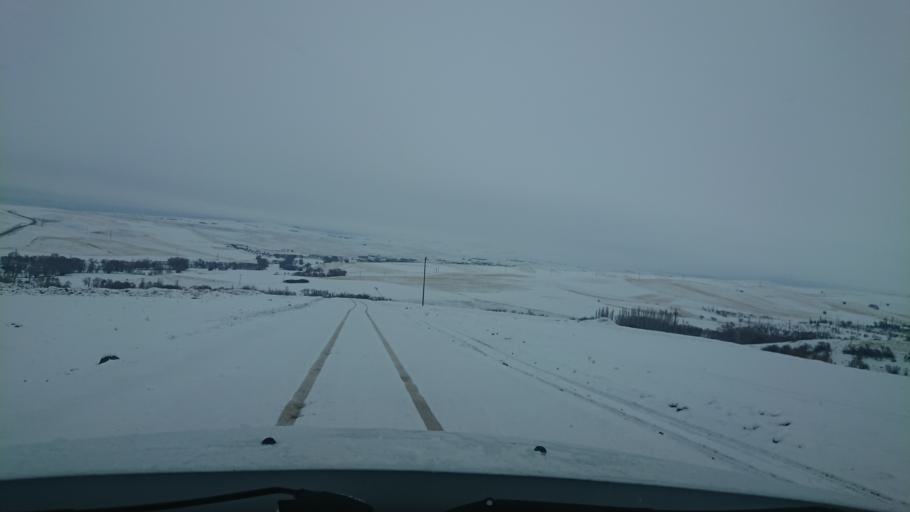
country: TR
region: Aksaray
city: Agacoren
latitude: 38.7534
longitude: 33.8759
